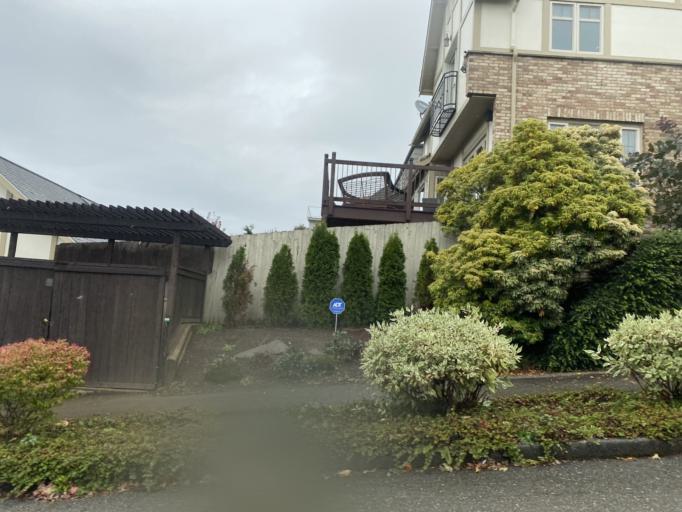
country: US
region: Washington
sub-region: King County
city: Seattle
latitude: 47.6447
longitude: -122.3935
